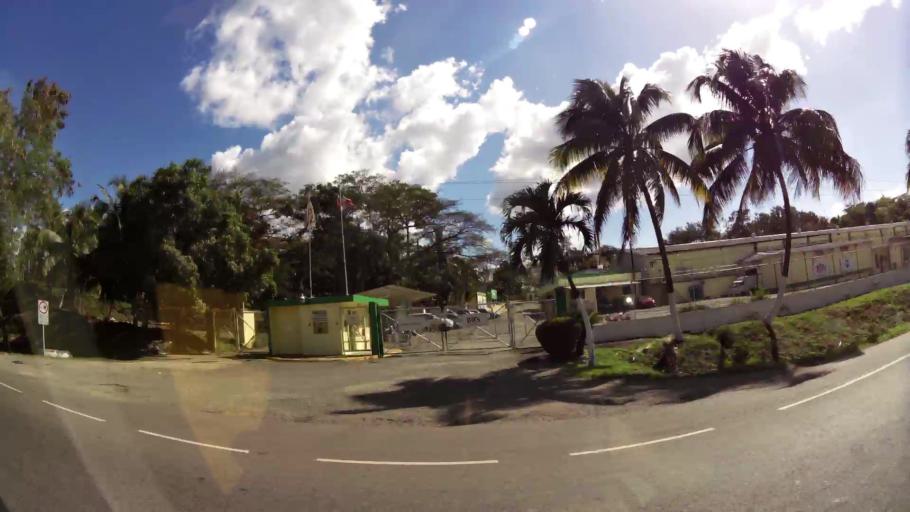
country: DO
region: Santo Domingo
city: Santo Domingo Oeste
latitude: 18.5607
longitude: -70.0620
